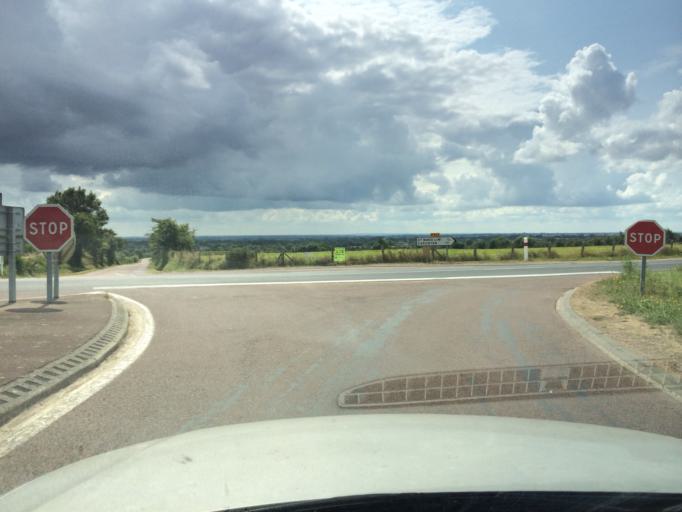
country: FR
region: Lower Normandy
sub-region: Departement de la Manche
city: Saint-Hilaire-Petitville
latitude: 49.3889
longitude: -1.2174
